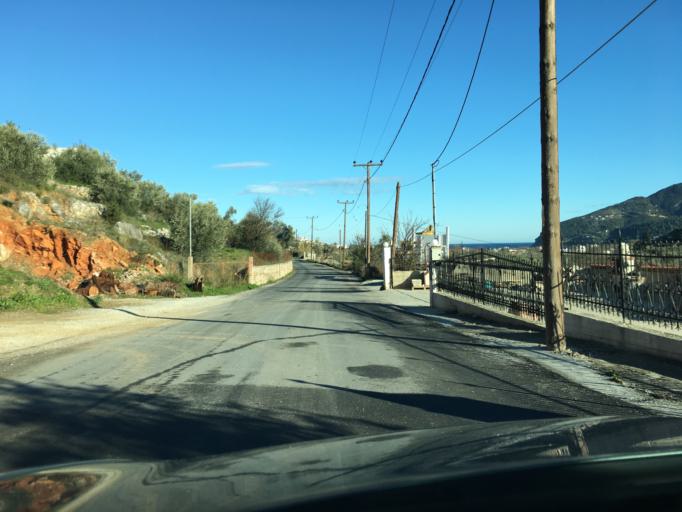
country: GR
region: Thessaly
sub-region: Nomos Magnisias
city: Skopelos
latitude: 39.1060
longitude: 23.7226
